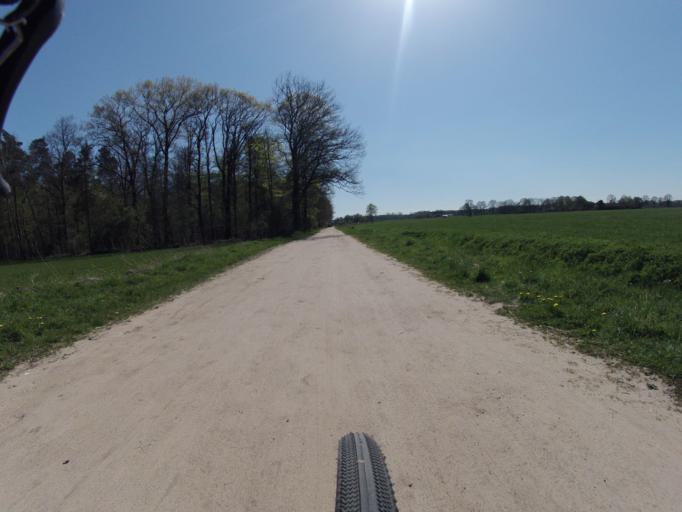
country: NL
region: Overijssel
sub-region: Gemeente Oldenzaal
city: Oldenzaal
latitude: 52.2681
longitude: 6.9483
